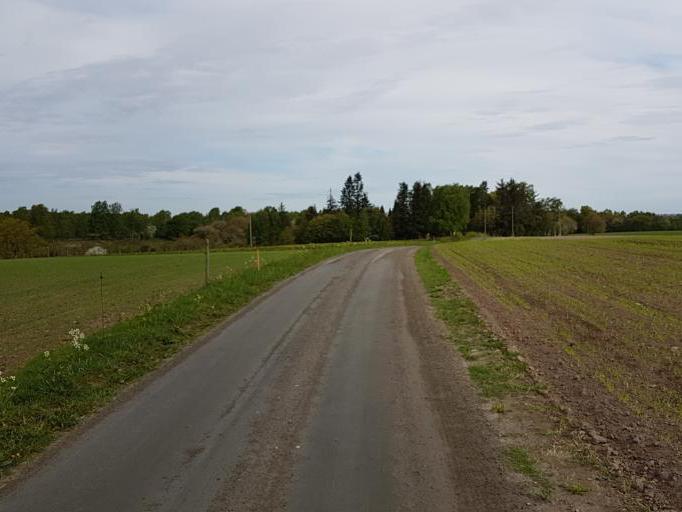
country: SE
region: Skane
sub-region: Lunds Kommun
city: Veberod
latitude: 55.6052
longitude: 13.5165
